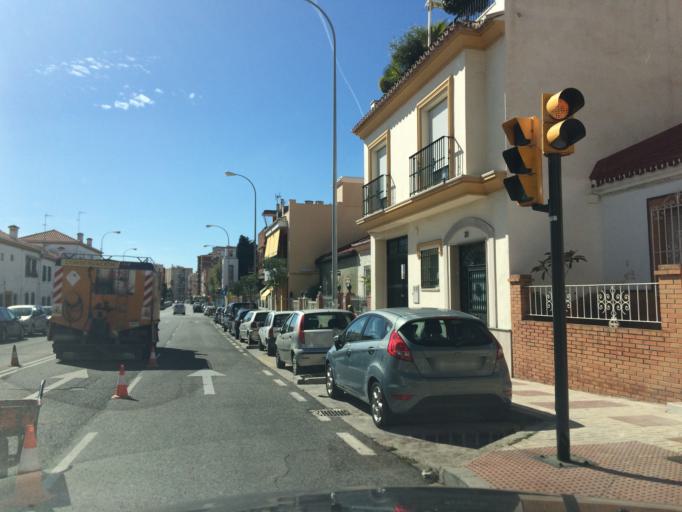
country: ES
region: Andalusia
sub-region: Provincia de Malaga
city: Malaga
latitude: 36.7263
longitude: -4.4388
